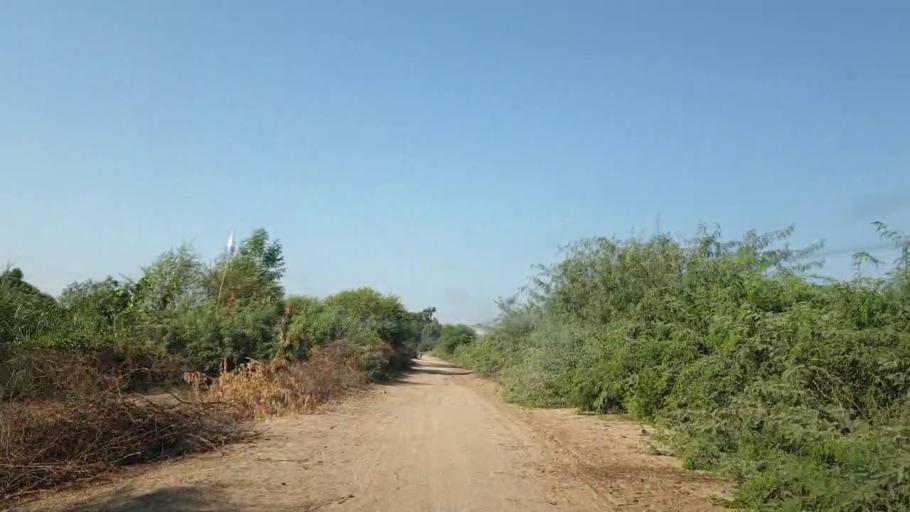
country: PK
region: Sindh
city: Tando Jam
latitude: 25.3717
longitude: 68.5690
